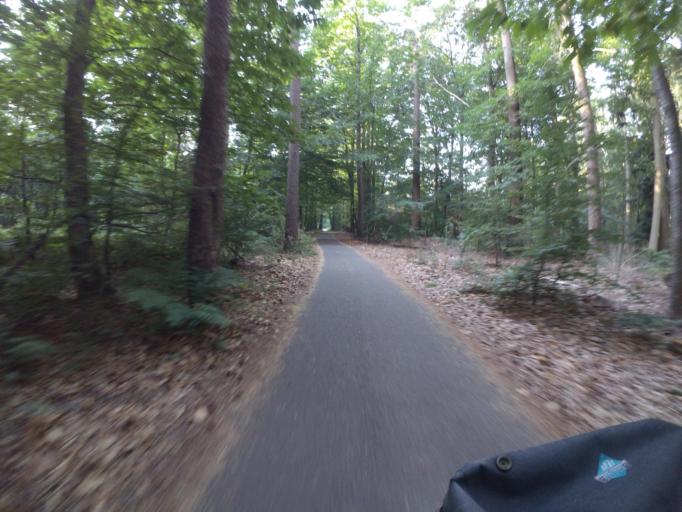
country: NL
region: Drenthe
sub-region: Gemeente Westerveld
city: Dwingeloo
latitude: 52.9470
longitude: 6.3398
